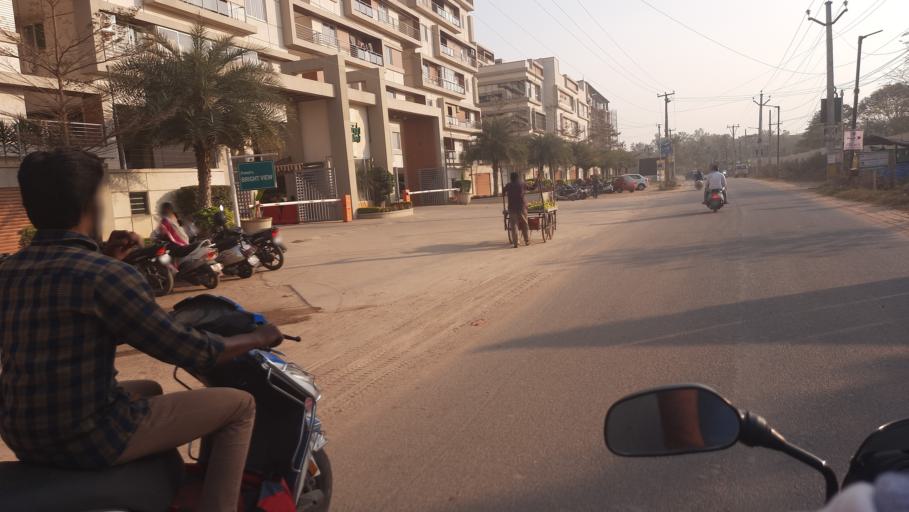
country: IN
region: Telangana
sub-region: Rangareddi
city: Secunderabad
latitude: 17.5202
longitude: 78.5410
